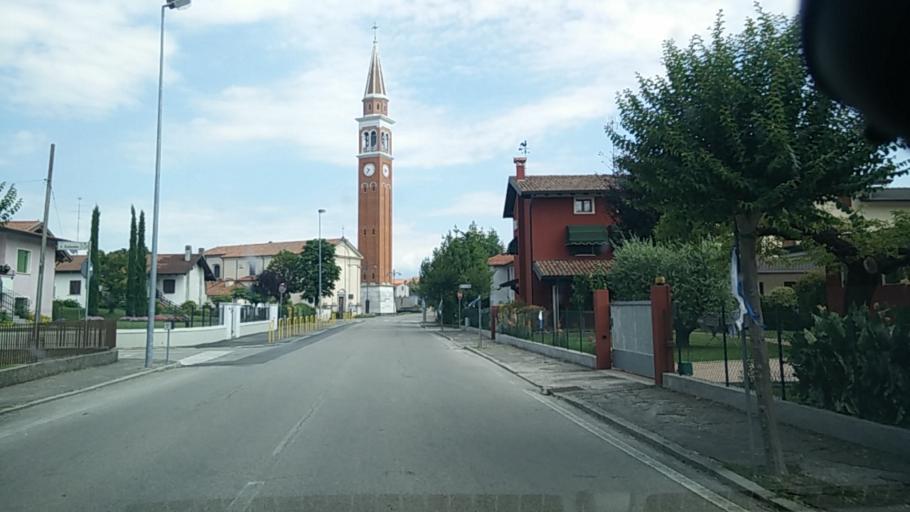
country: IT
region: Friuli Venezia Giulia
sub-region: Provincia di Pordenone
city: Puia-Villanova
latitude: 45.8410
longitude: 12.5661
